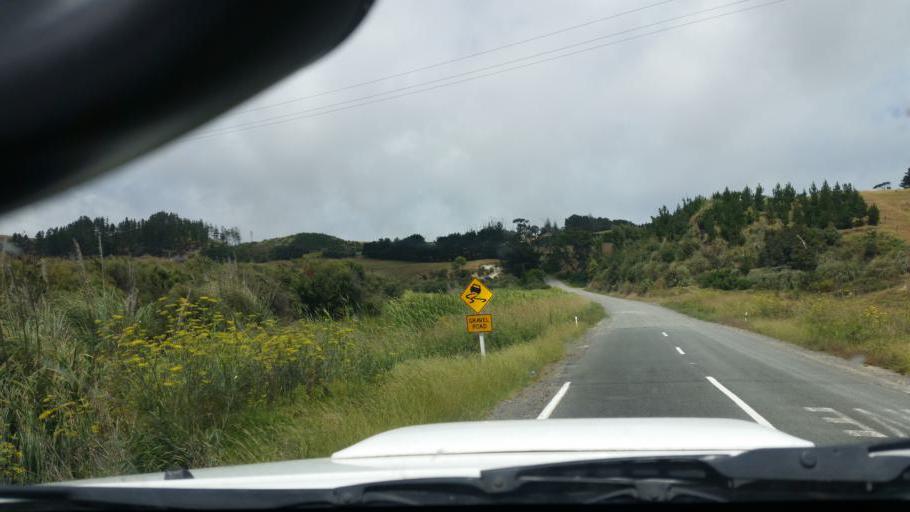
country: NZ
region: Northland
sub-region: Kaipara District
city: Dargaville
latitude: -35.8347
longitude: 173.6611
